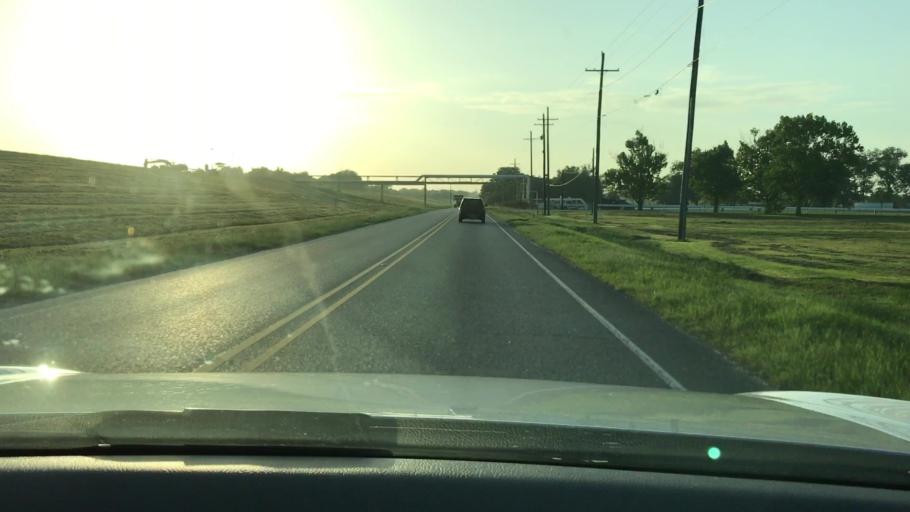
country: US
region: Louisiana
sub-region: Iberville Parish
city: Plaquemine
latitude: 30.2730
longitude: -91.1833
